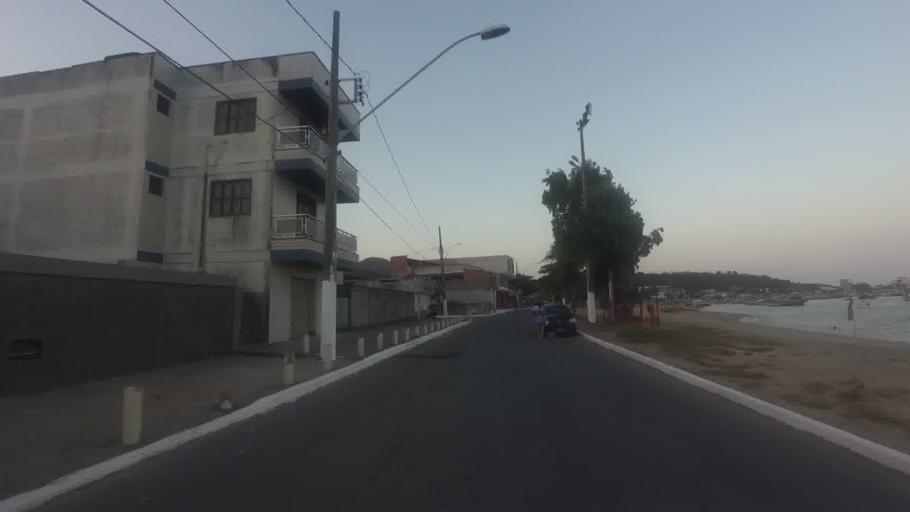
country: BR
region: Espirito Santo
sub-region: Piuma
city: Piuma
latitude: -20.8930
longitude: -40.7737
